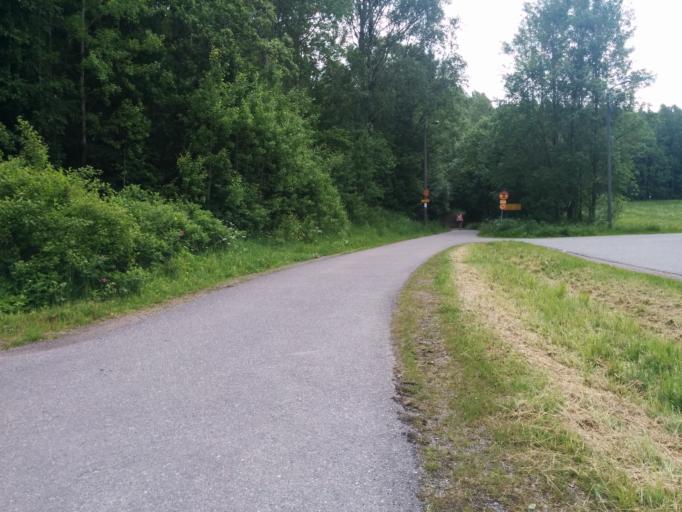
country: FI
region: Uusimaa
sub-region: Helsinki
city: Vantaa
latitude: 60.2370
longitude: 25.1365
